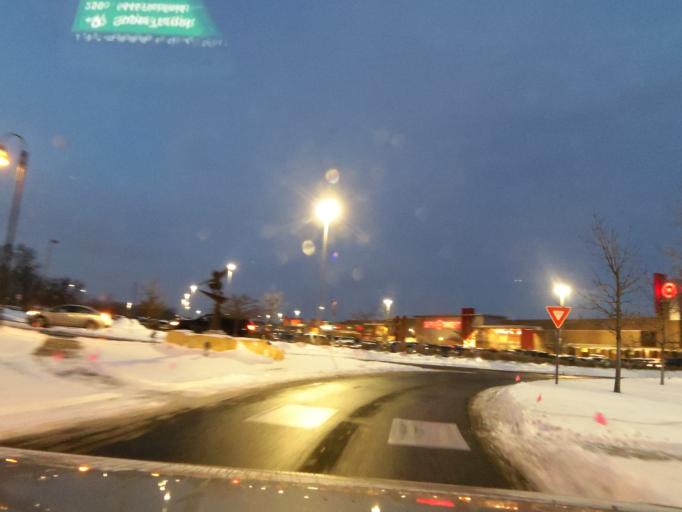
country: US
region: Minnesota
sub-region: Hennepin County
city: Richfield
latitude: 44.8846
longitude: -93.2501
